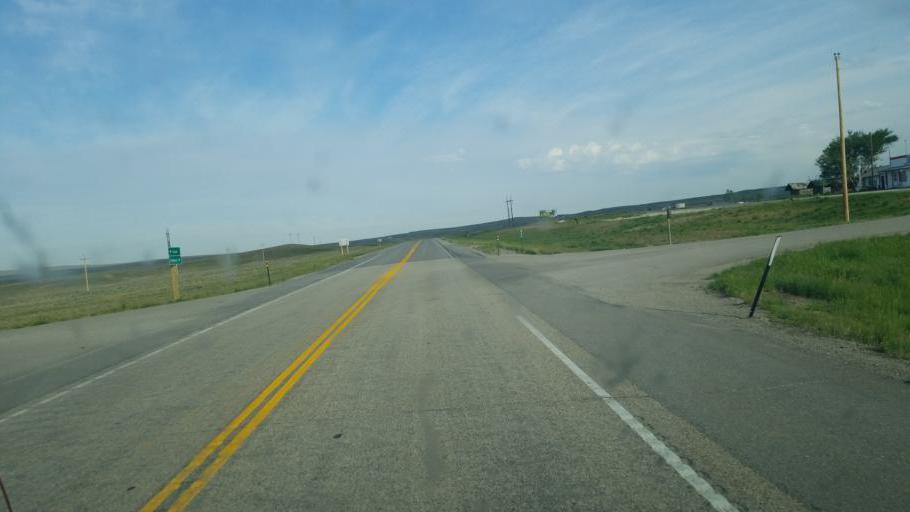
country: US
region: Wyoming
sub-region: Natrona County
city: Mills
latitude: 43.0706
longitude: -107.1959
